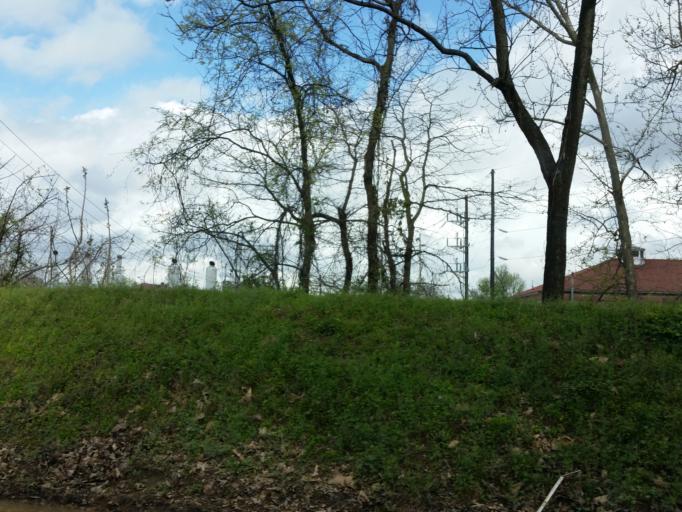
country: US
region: Missouri
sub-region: Butler County
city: Poplar Bluff
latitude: 36.7590
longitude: -90.3879
